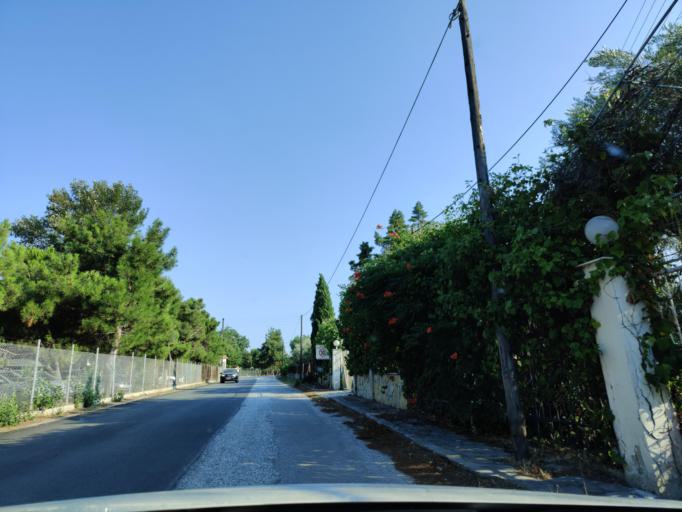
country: GR
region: East Macedonia and Thrace
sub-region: Nomos Kavalas
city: Nea Peramos
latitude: 40.8294
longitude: 24.3049
